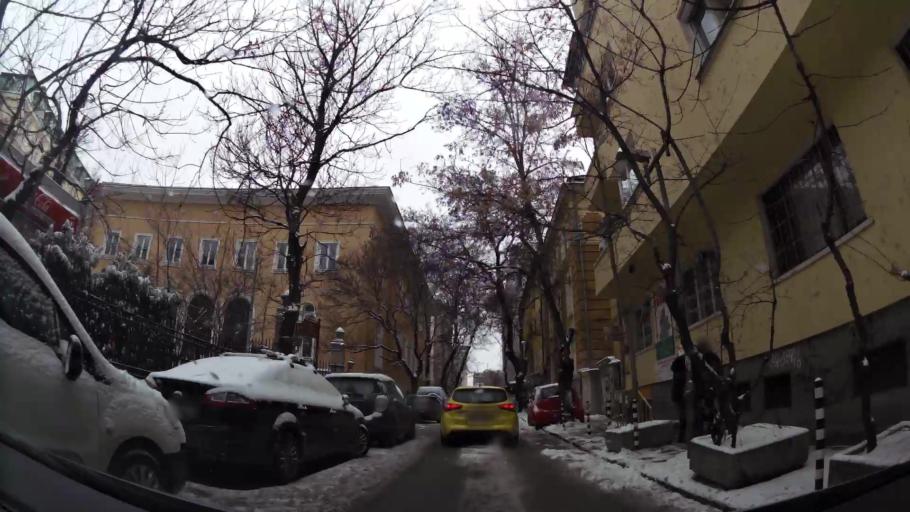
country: BG
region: Sofia-Capital
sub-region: Stolichna Obshtina
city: Sofia
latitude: 42.6931
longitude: 23.3358
